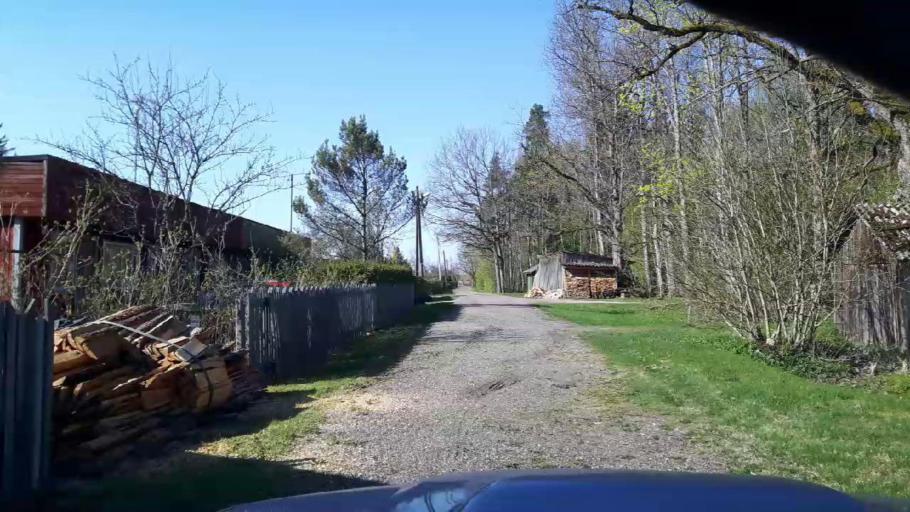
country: EE
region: Paernumaa
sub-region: Sindi linn
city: Sindi
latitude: 58.4516
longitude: 24.7699
